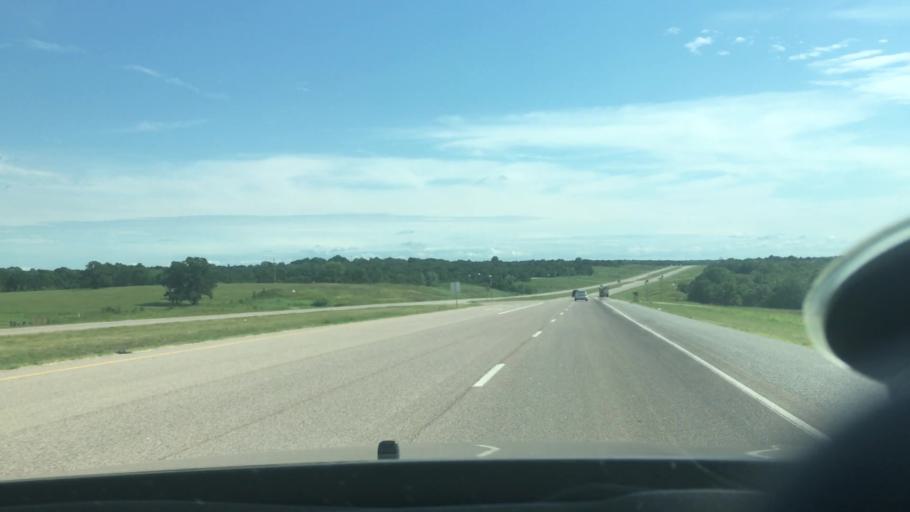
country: US
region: Oklahoma
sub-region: Pontotoc County
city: Byng
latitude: 34.8915
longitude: -96.6753
